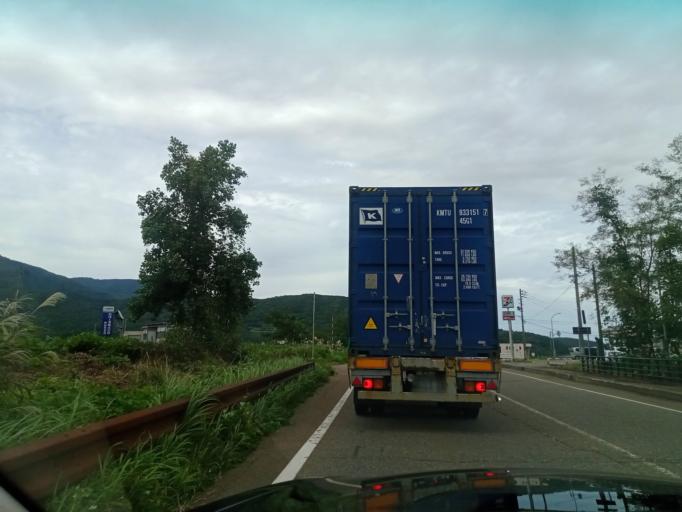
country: JP
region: Niigata
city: Arai
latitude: 37.0195
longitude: 138.2278
